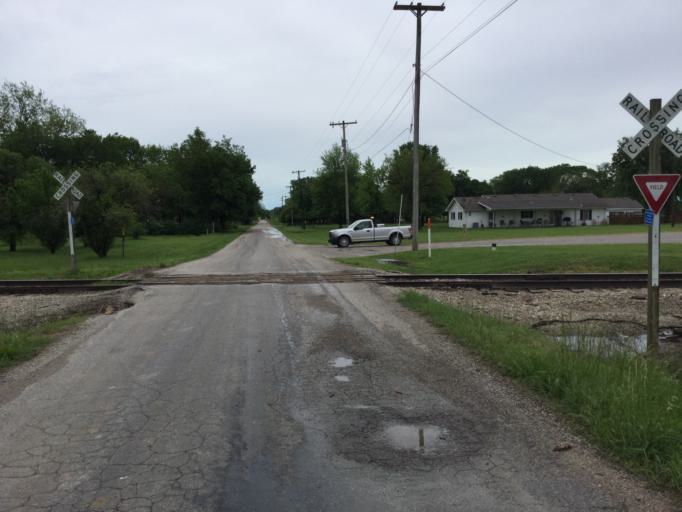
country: US
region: Kansas
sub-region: Labette County
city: Altamont
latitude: 37.1917
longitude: -95.3043
